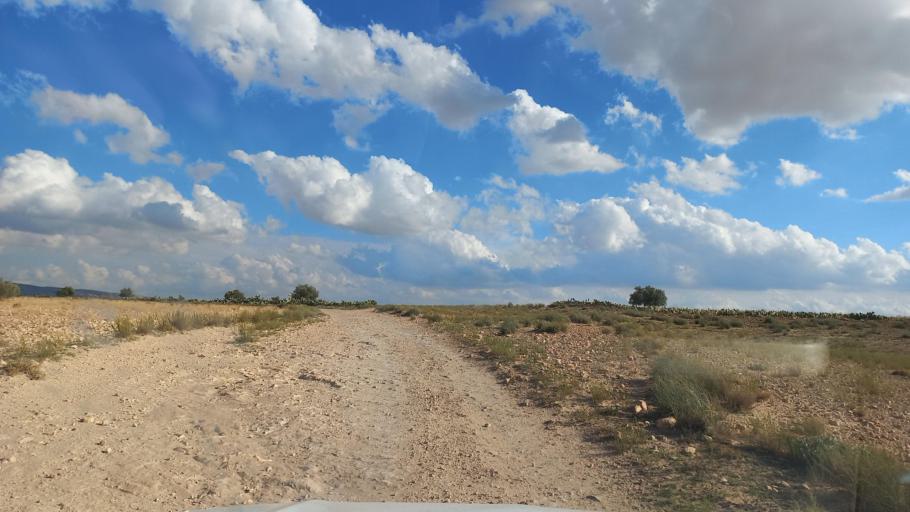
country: TN
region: Al Qasrayn
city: Sbiba
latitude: 35.3947
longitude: 9.0402
